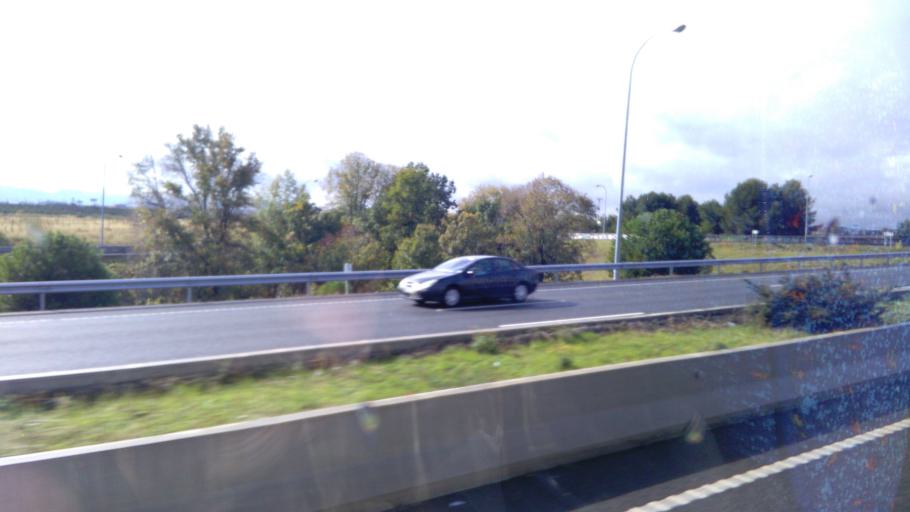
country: ES
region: Madrid
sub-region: Provincia de Madrid
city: Villaverde
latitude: 40.3649
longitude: -3.7177
